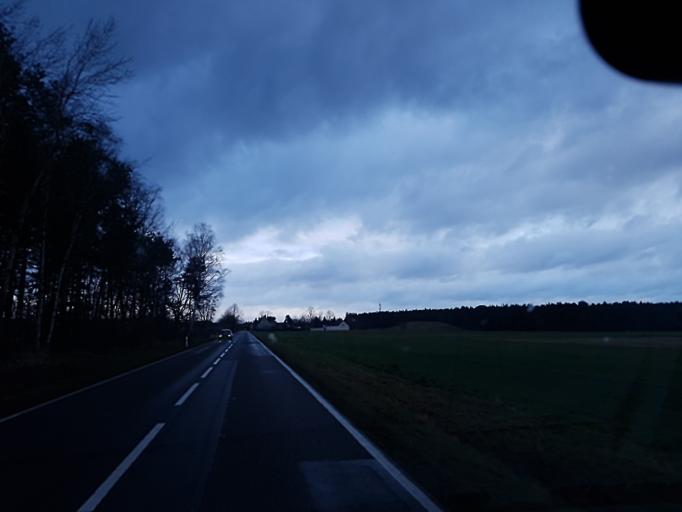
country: DE
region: Brandenburg
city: Finsterwalde
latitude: 51.5611
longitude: 13.6730
